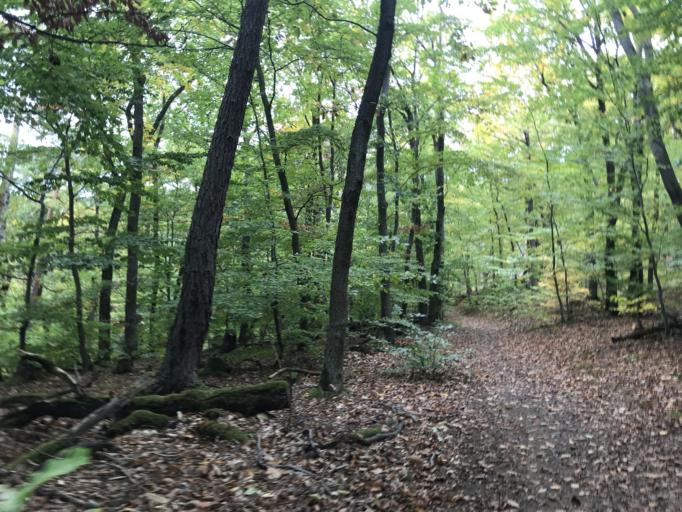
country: DE
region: Rheinland-Pfalz
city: Bolanden
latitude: 49.6526
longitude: 7.9816
